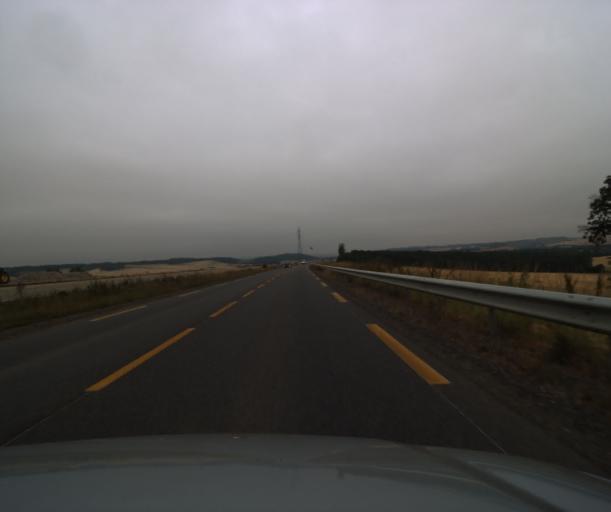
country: FR
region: Midi-Pyrenees
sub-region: Departement du Gers
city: Preignan
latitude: 43.6486
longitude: 0.6905
